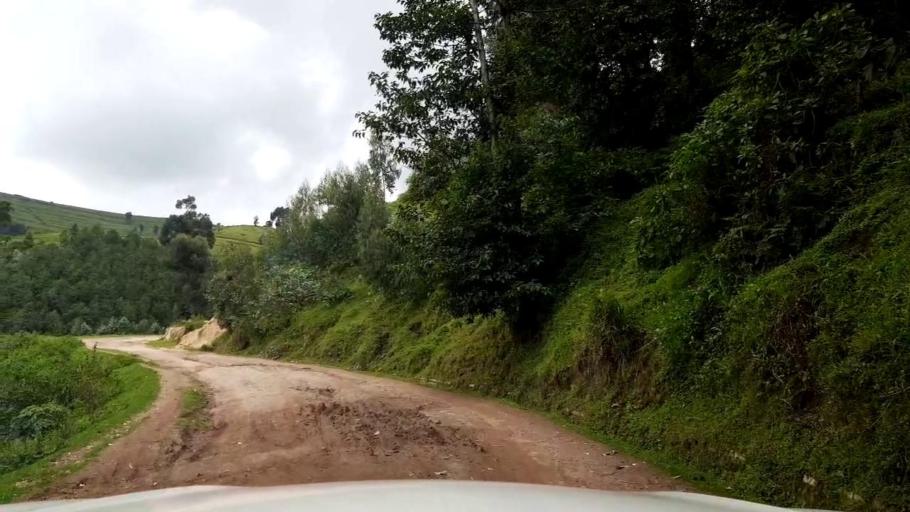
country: RW
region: Western Province
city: Gisenyi
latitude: -1.6496
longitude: 29.4133
